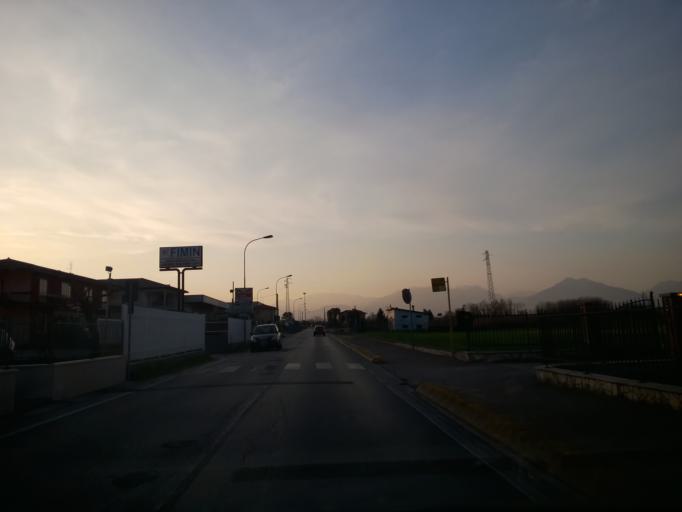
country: IT
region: Veneto
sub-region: Provincia di Vicenza
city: Villaverla
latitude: 45.6309
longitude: 11.4952
